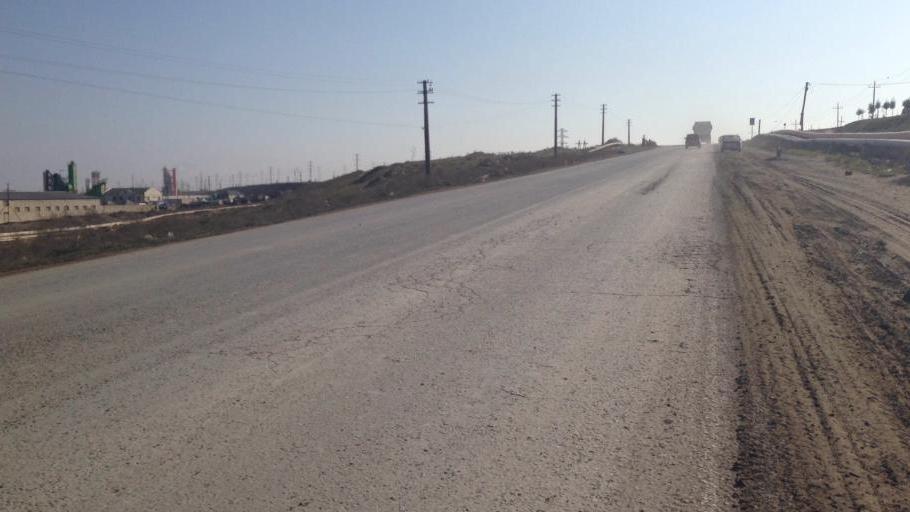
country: AZ
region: Baki
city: Balakhani
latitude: 40.4646
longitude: 49.8881
